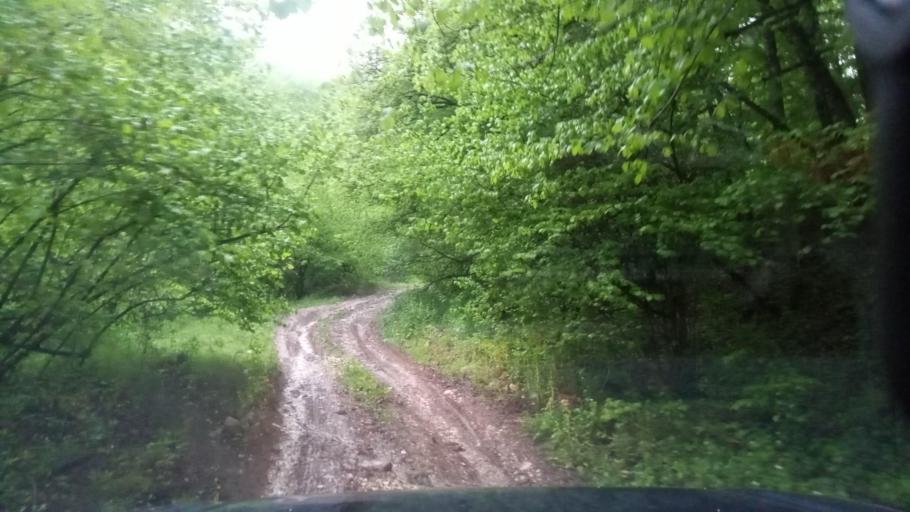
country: RU
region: Kabardino-Balkariya
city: Belaya Rechka
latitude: 43.4074
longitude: 43.4649
